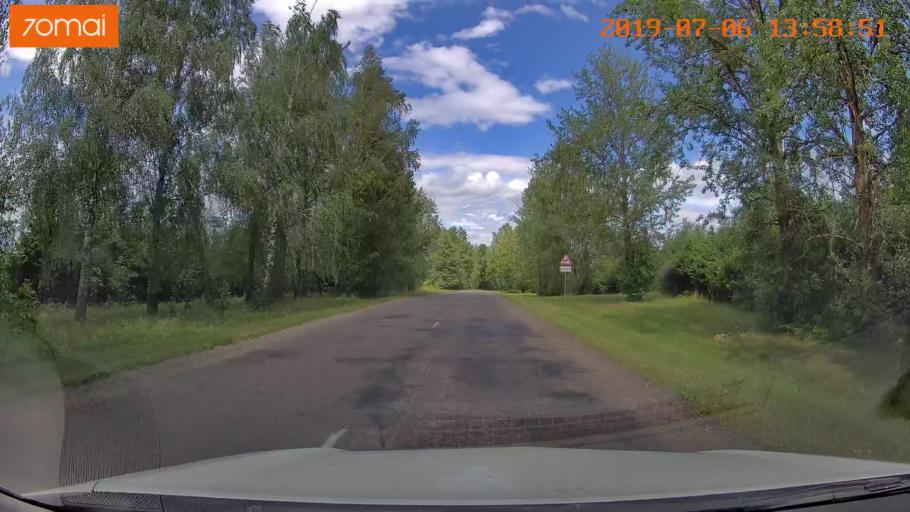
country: BY
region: Minsk
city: Ivyanyets
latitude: 53.7888
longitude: 26.8104
